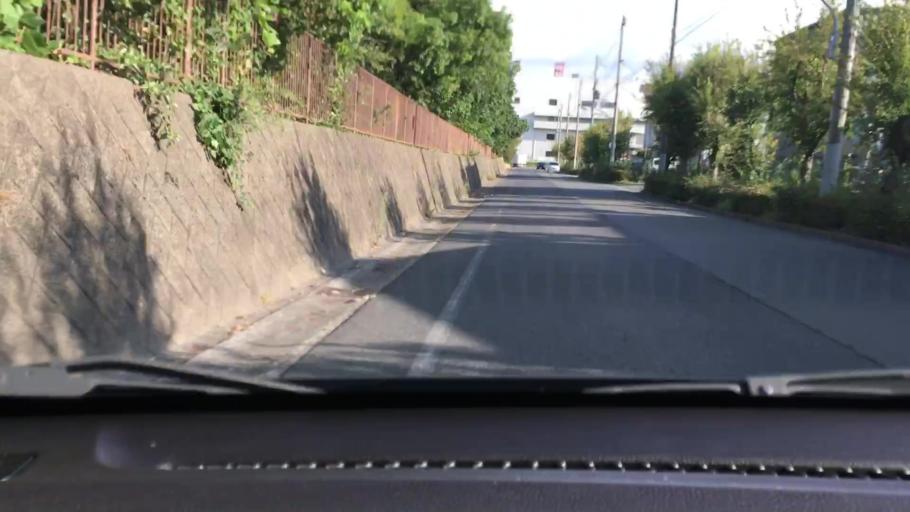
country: JP
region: Hyogo
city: Ashiya
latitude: 34.6924
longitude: 135.2751
